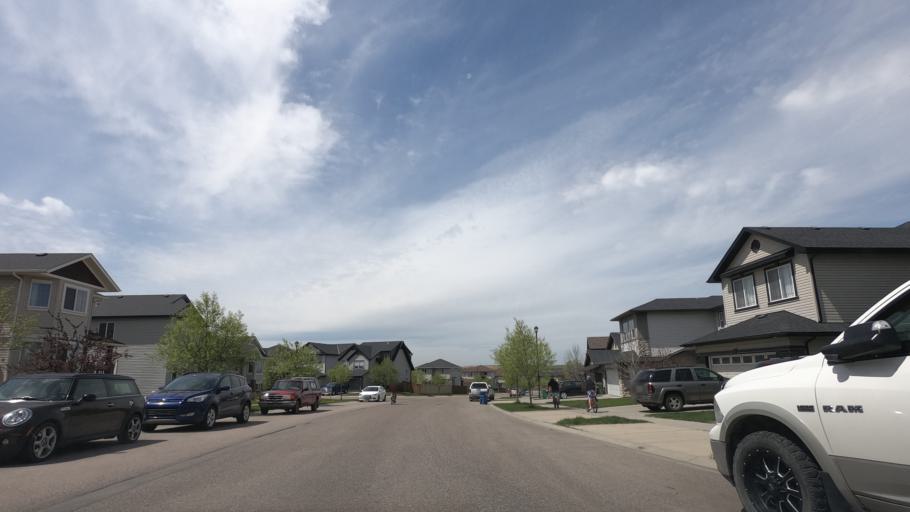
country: CA
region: Alberta
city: Airdrie
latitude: 51.2662
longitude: -114.0280
